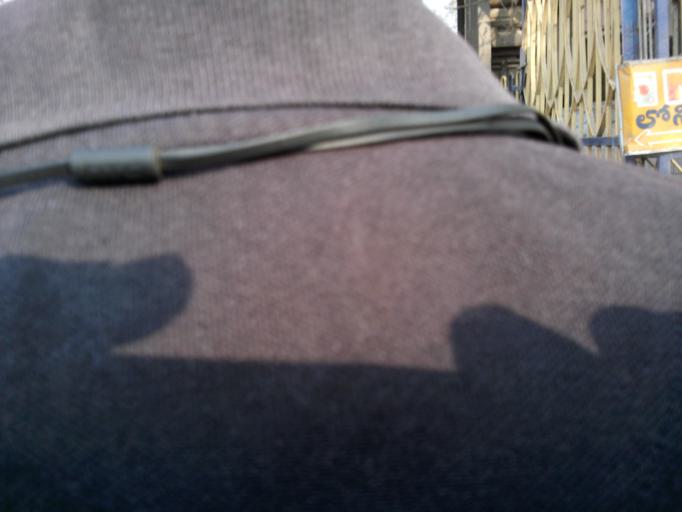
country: IN
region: Andhra Pradesh
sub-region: Krishna
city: Vijayawada
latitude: 16.5132
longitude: 80.6038
